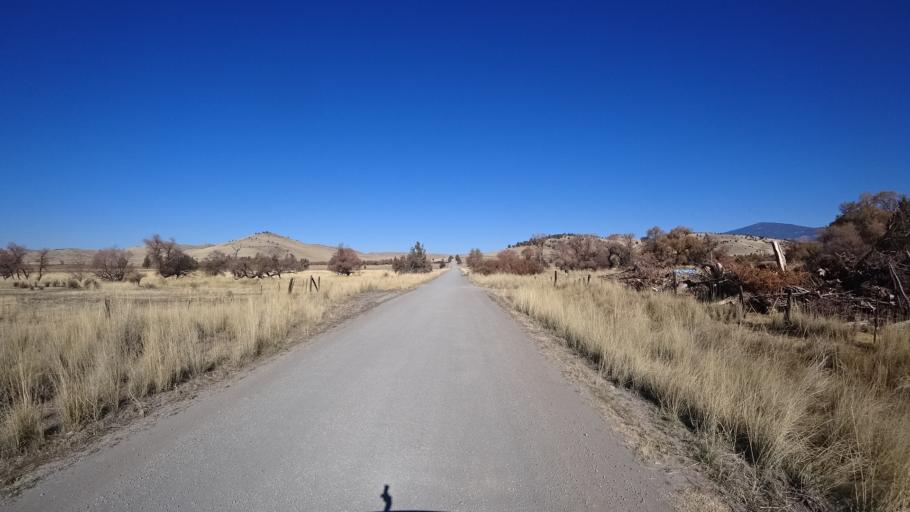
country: US
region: California
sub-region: Siskiyou County
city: Montague
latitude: 41.7238
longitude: -122.3696
